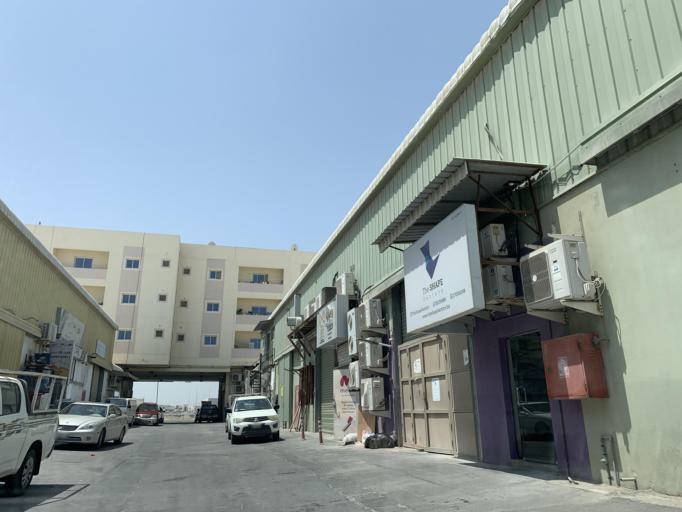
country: BH
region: Northern
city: Madinat `Isa
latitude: 26.1946
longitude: 50.5446
